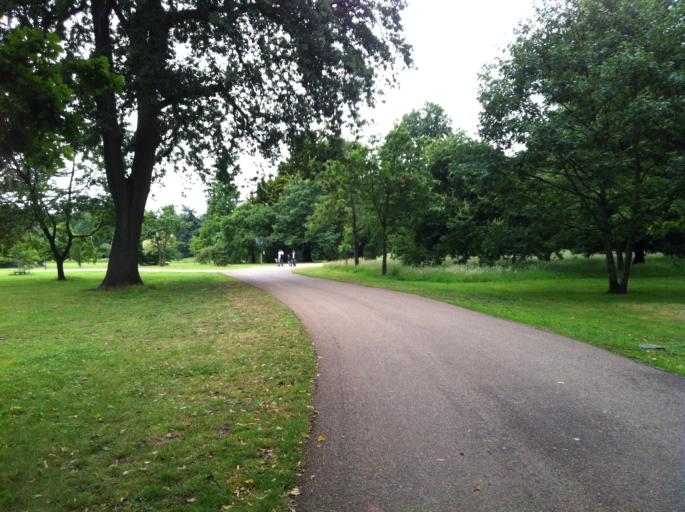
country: GB
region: Wales
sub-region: Cardiff
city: Cardiff
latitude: 51.4855
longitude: -3.1848
